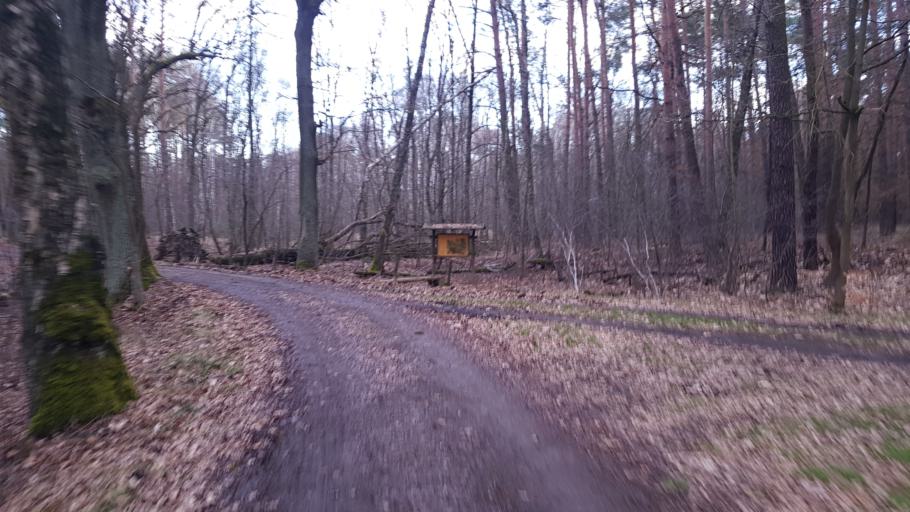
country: DE
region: Brandenburg
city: Falkenberg
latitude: 51.5811
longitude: 13.3088
